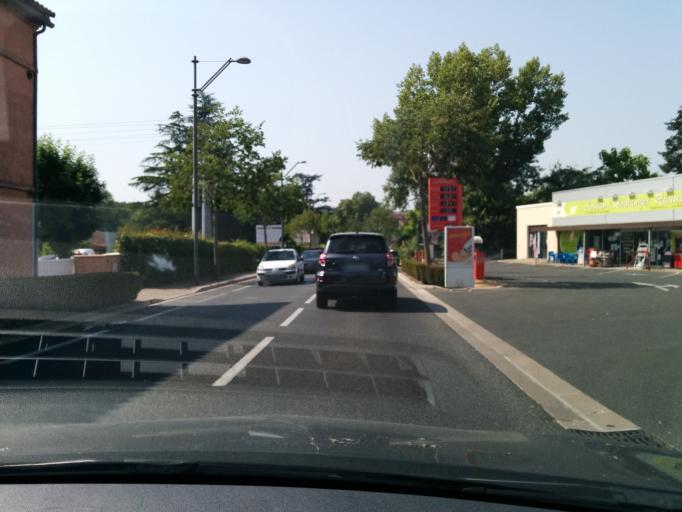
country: FR
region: Midi-Pyrenees
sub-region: Departement du Tarn
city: Albi
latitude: 43.9452
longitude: 2.1333
